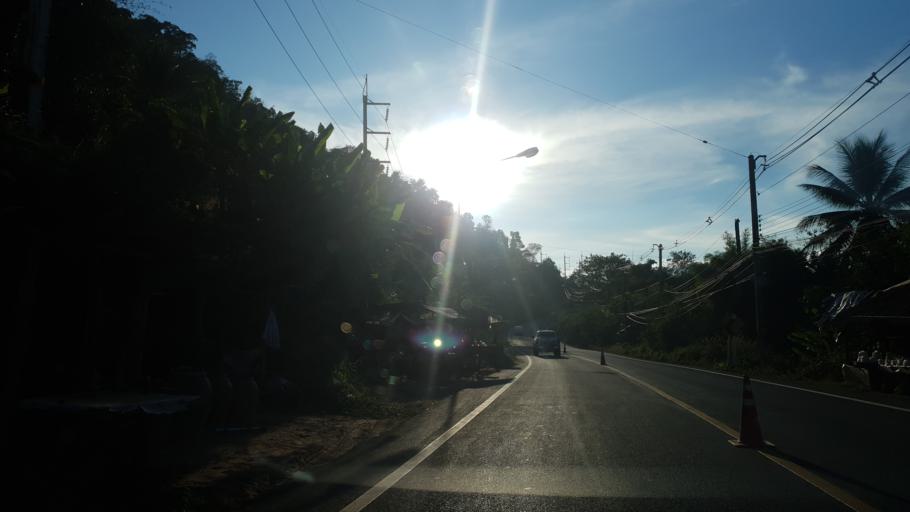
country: TH
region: Loei
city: Dan Sai
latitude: 17.2314
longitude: 101.0514
